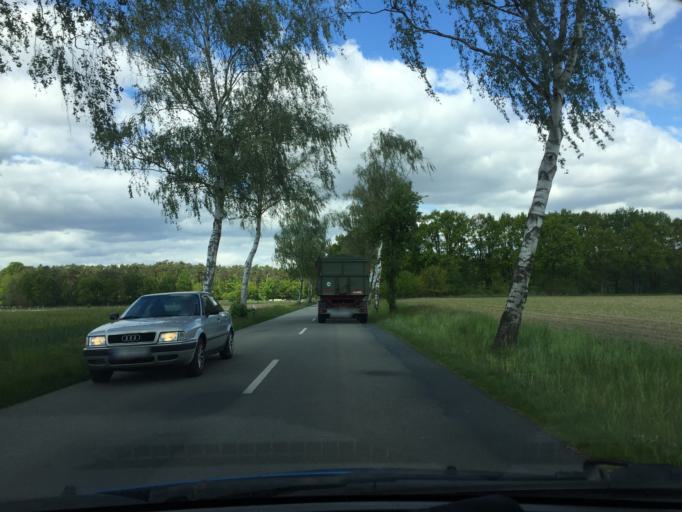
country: DE
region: Lower Saxony
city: Suderburg
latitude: 52.9217
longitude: 10.5009
